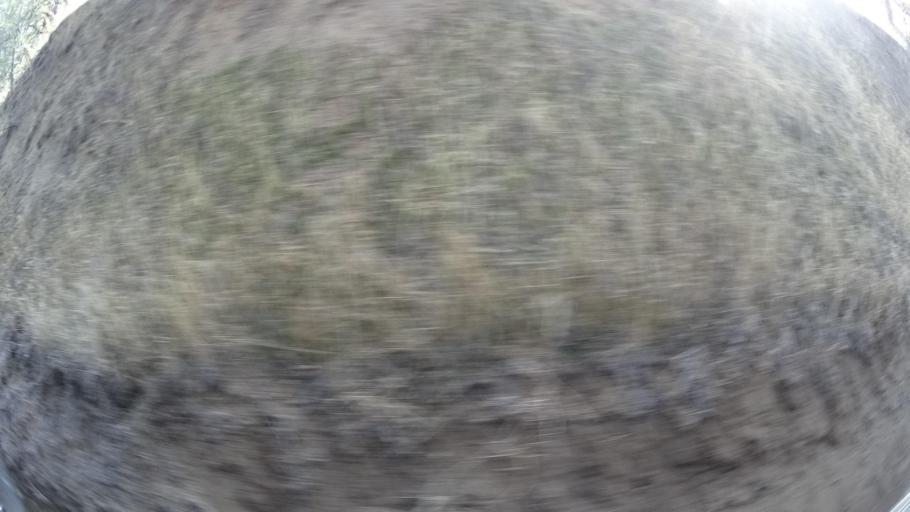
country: US
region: California
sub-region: Kern County
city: Alta Sierra
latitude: 35.6616
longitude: -118.7465
